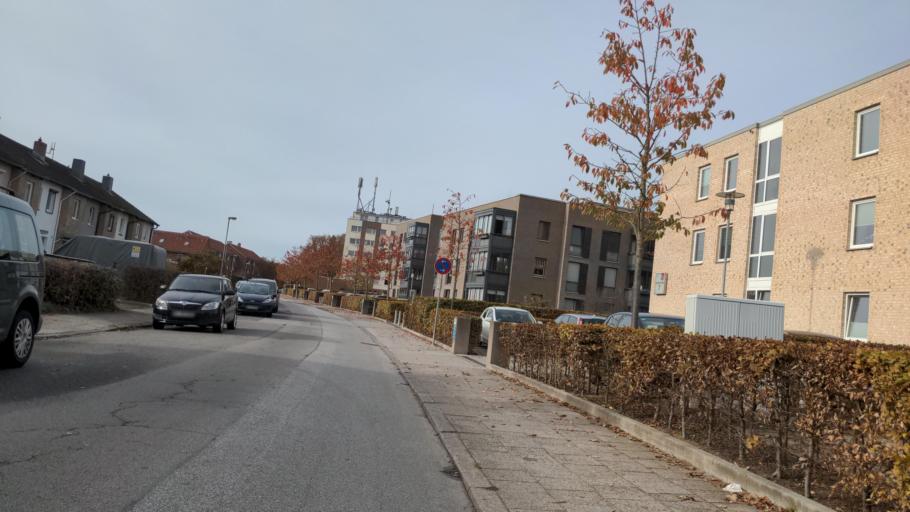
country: DE
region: Mecklenburg-Vorpommern
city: Selmsdorf
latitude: 53.9198
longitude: 10.8205
